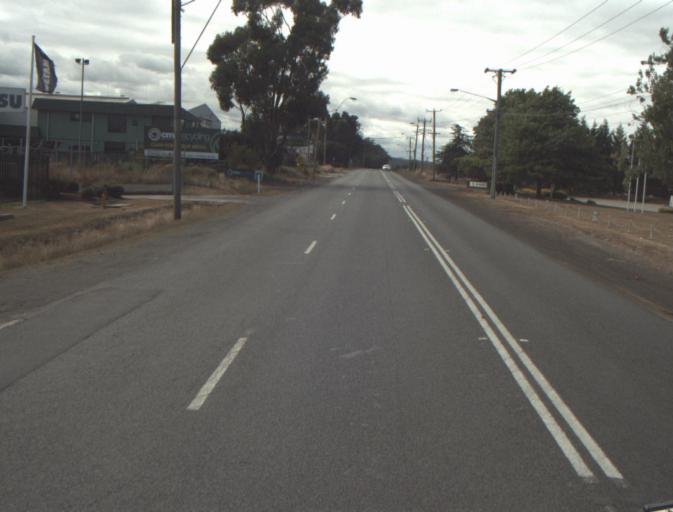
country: AU
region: Tasmania
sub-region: Launceston
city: Mayfield
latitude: -41.3749
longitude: 147.1205
